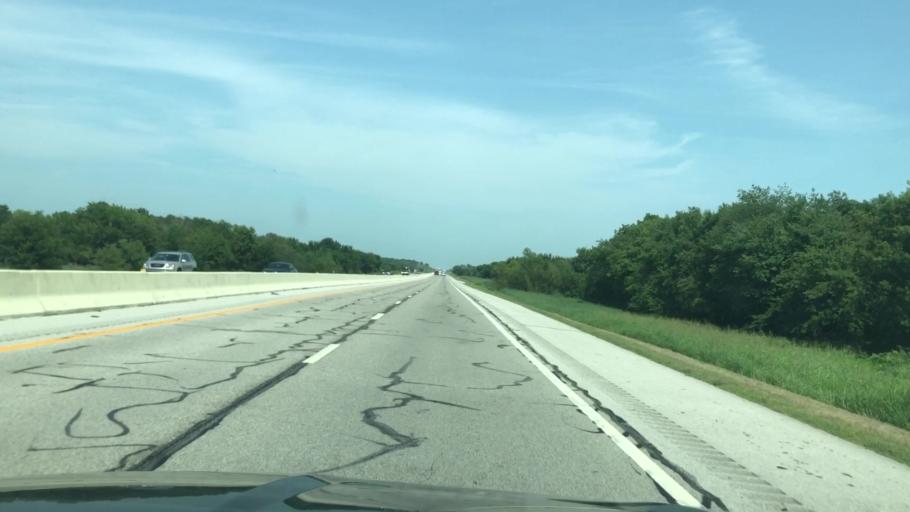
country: US
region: Oklahoma
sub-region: Rogers County
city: Chelsea
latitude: 36.4743
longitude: -95.3266
